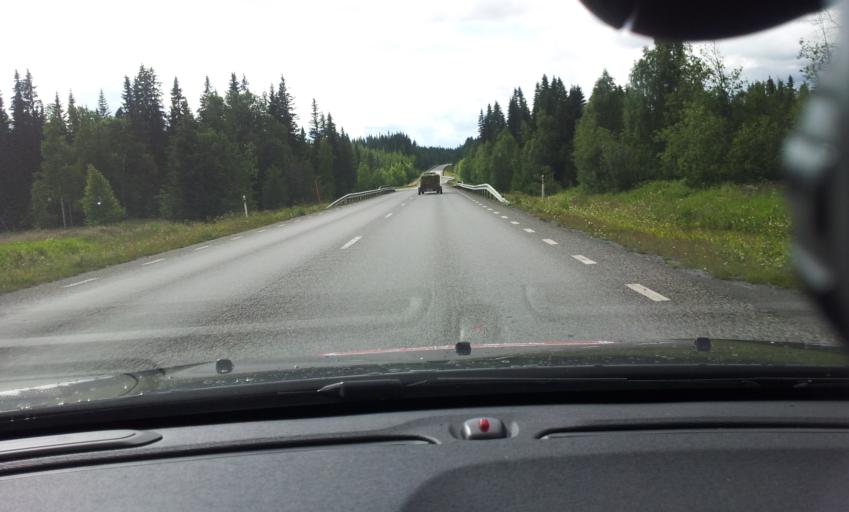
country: SE
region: Jaemtland
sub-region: Krokoms Kommun
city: Valla
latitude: 63.3118
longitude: 13.7475
